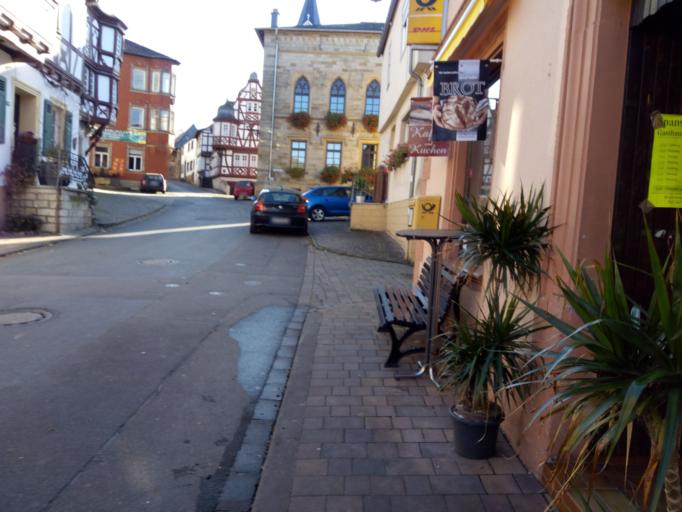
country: DE
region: Rheinland-Pfalz
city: Monzingen
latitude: 49.8002
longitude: 7.5911
